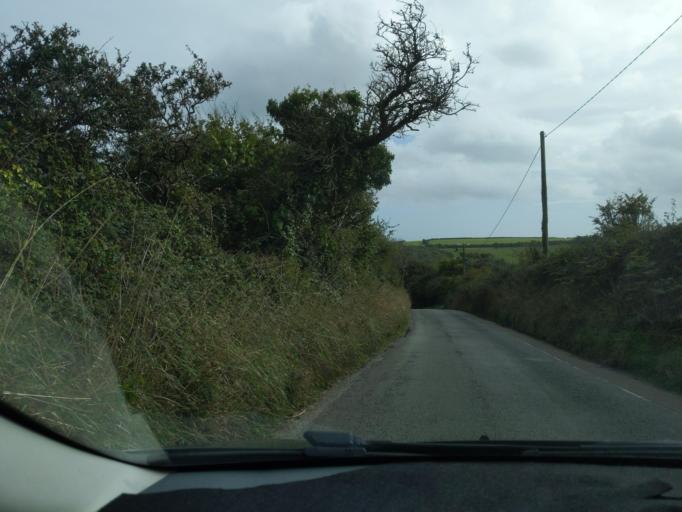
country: GB
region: England
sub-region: Cornwall
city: Mevagissey
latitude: 50.2436
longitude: -4.8001
